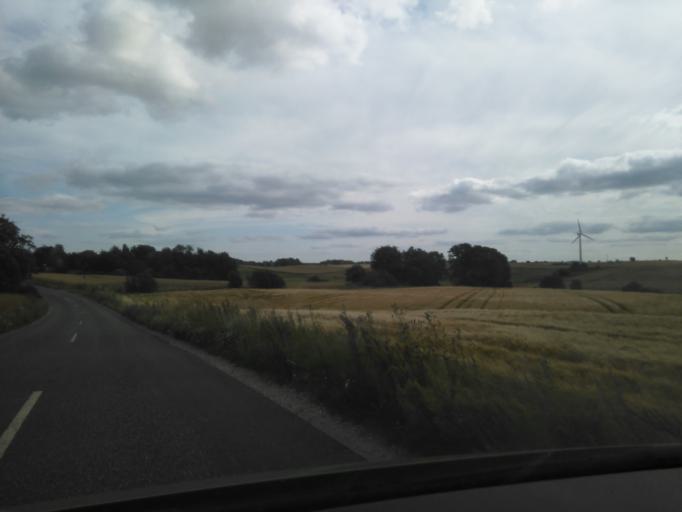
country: DK
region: Central Jutland
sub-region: Arhus Kommune
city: Solbjerg
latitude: 56.0762
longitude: 10.0882
